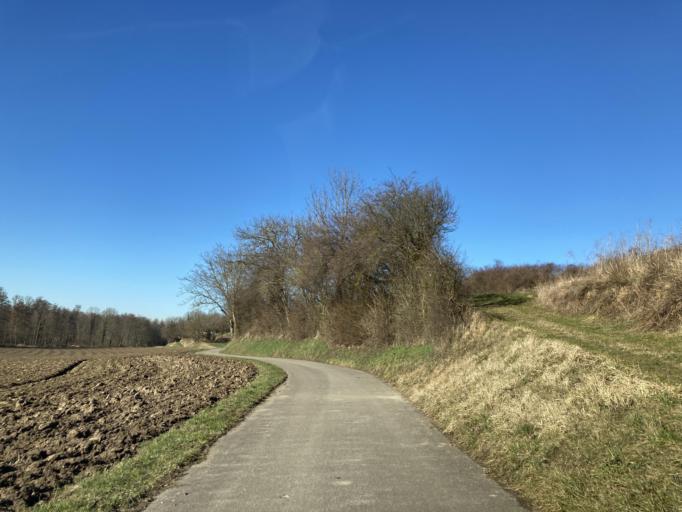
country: DE
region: Baden-Wuerttemberg
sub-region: Freiburg Region
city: Eichstetten
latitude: 48.0786
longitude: 7.7751
